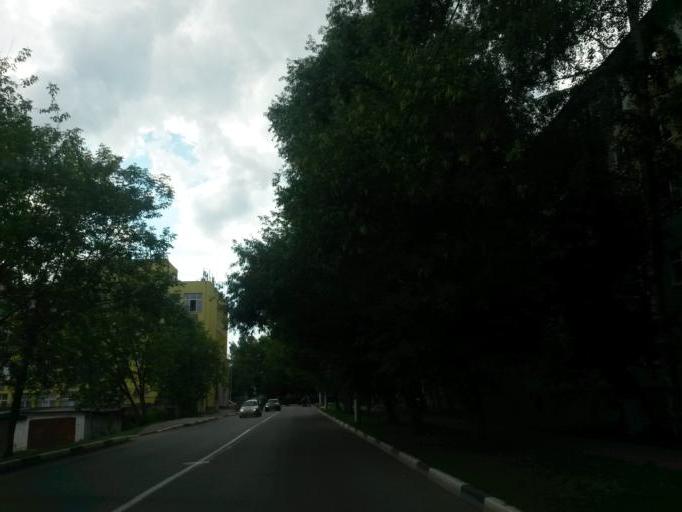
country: RU
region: Moskovskaya
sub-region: Chekhovskiy Rayon
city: Chekhov
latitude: 55.1516
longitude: 37.4699
